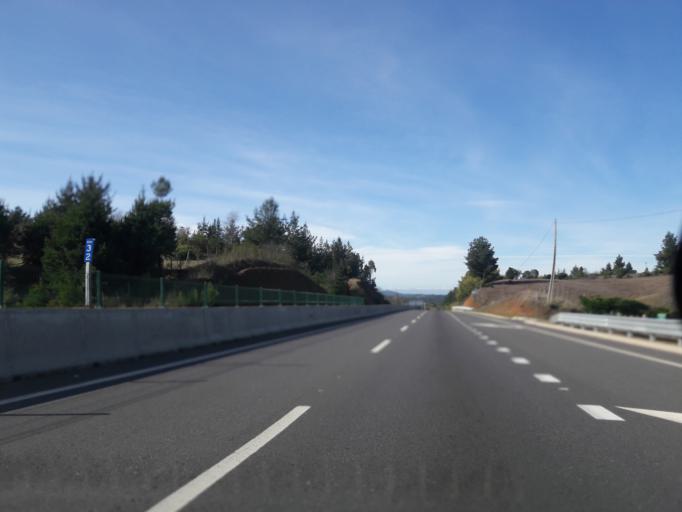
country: CL
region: Biobio
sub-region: Provincia de Biobio
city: Yumbel
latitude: -36.9636
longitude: -72.7079
